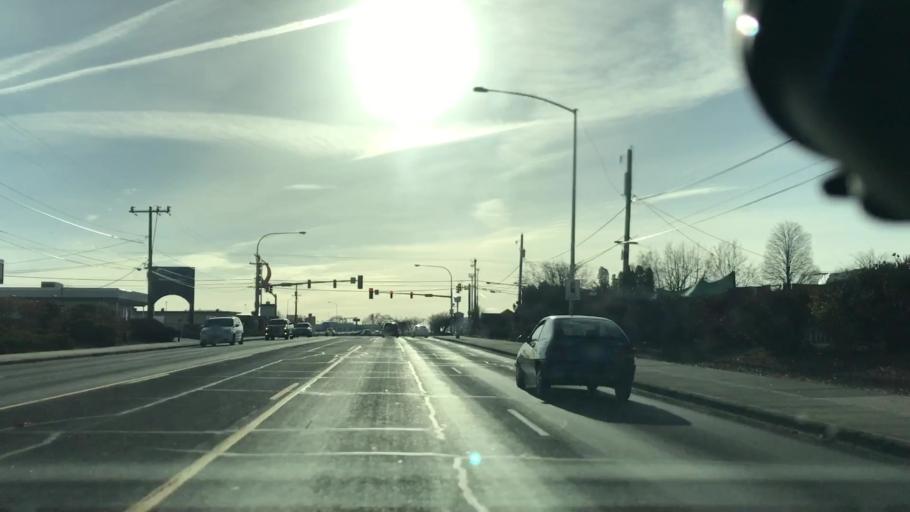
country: US
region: Washington
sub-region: Grant County
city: Moses Lake
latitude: 47.1221
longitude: -119.2679
